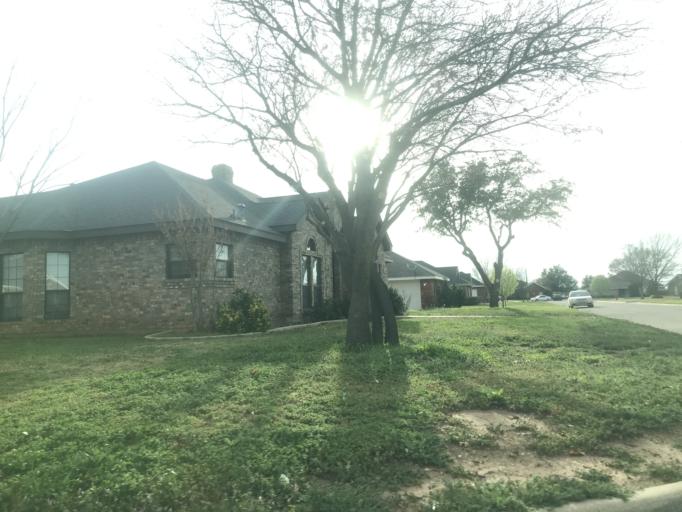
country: US
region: Texas
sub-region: Taylor County
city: Abilene
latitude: 32.3975
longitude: -99.7733
